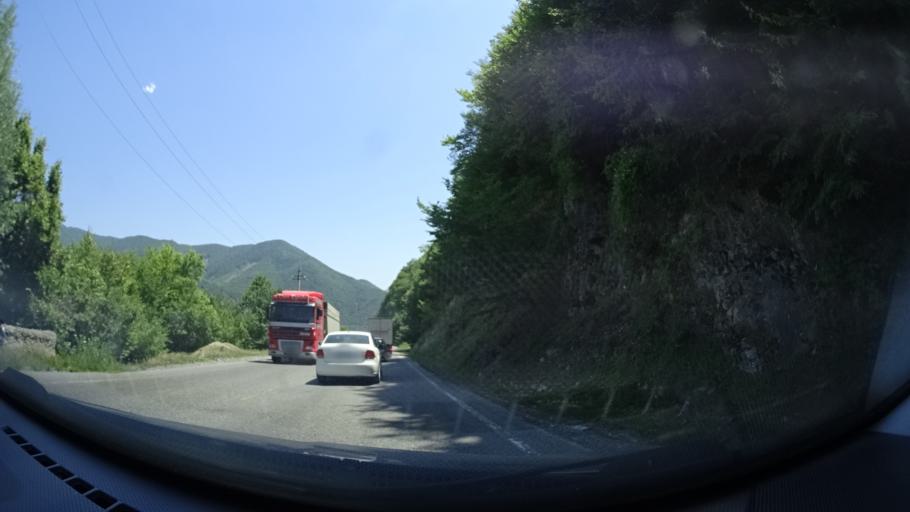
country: GE
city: Zhinvali
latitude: 42.1510
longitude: 44.7581
